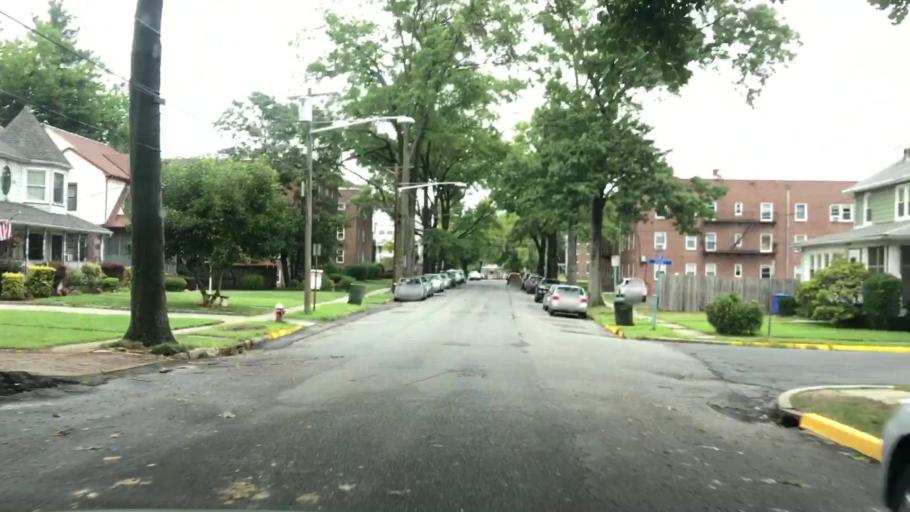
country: US
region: New Jersey
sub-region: Bergen County
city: Rutherford
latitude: 40.8323
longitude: -74.1094
